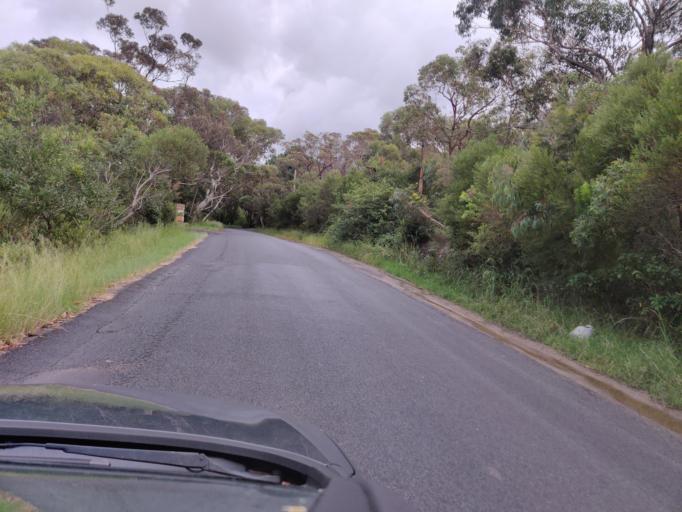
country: AU
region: New South Wales
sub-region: Pittwater
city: Ingleside
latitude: -33.6818
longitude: 151.2522
